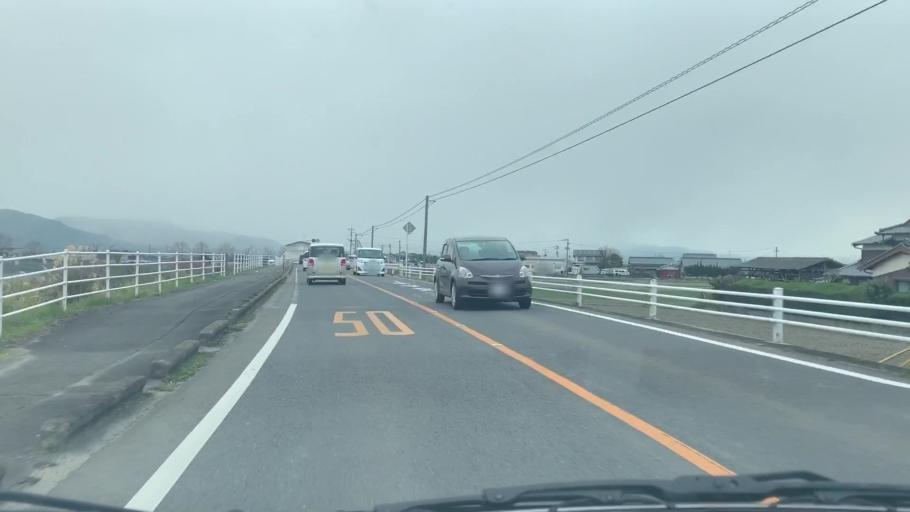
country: JP
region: Saga Prefecture
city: Saga-shi
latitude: 33.1882
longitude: 130.1933
